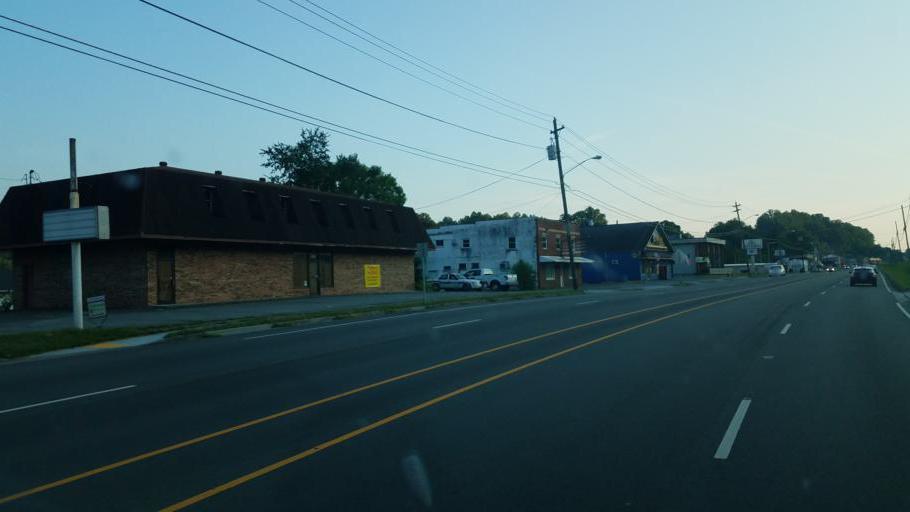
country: US
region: Virginia
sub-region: Scott County
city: Weber City
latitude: 36.6286
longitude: -82.5537
